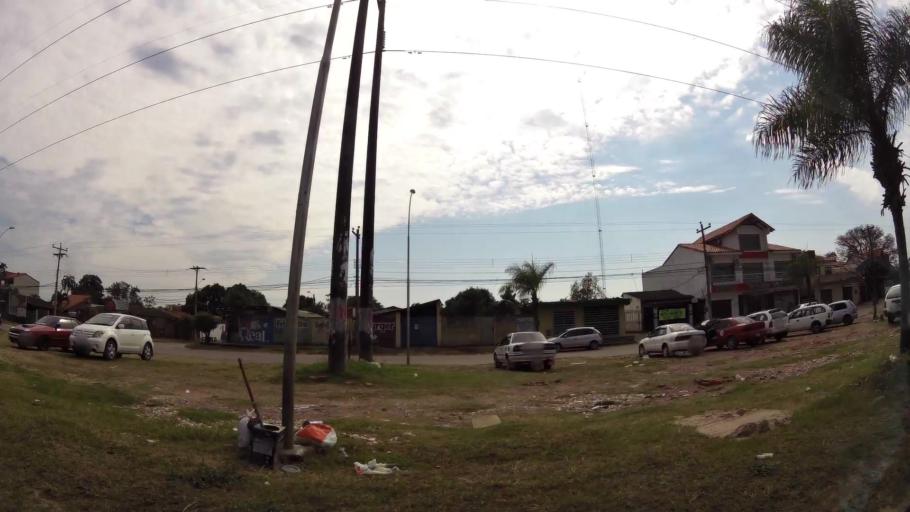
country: BO
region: Santa Cruz
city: Santa Cruz de la Sierra
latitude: -17.7438
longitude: -63.1629
